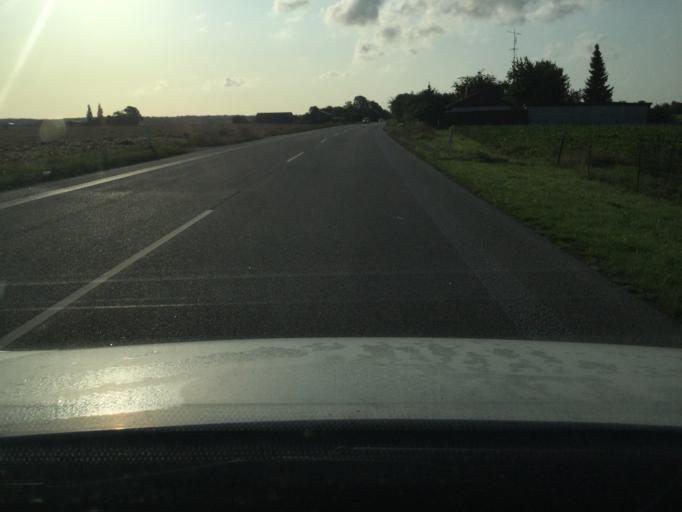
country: DK
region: Zealand
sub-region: Lolland Kommune
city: Rodby
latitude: 54.7643
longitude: 11.3159
